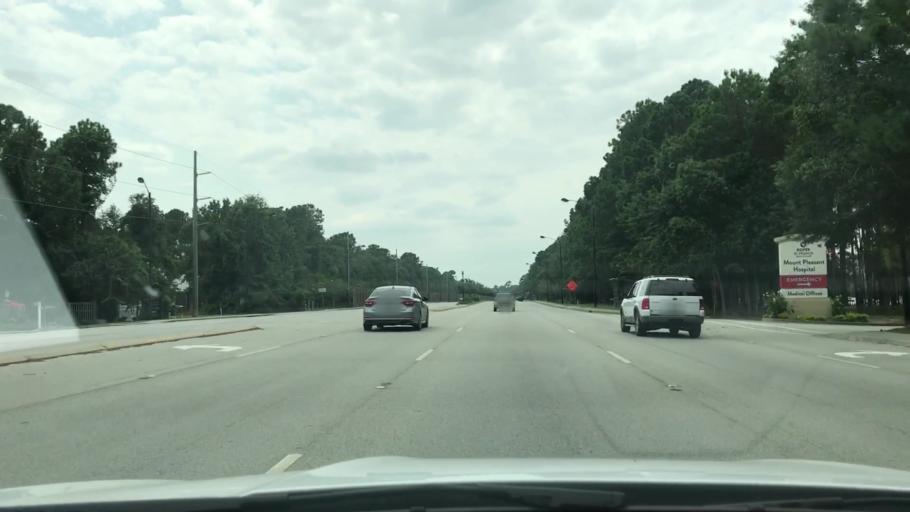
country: US
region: South Carolina
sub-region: Charleston County
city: Isle of Palms
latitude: 32.8788
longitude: -79.7647
